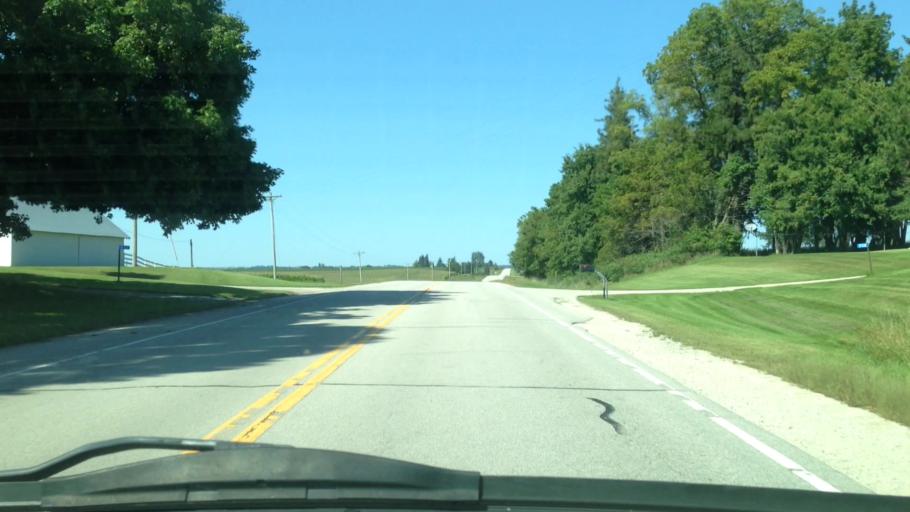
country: US
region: Minnesota
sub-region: Houston County
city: Spring Grove
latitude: 43.6075
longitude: -91.7903
